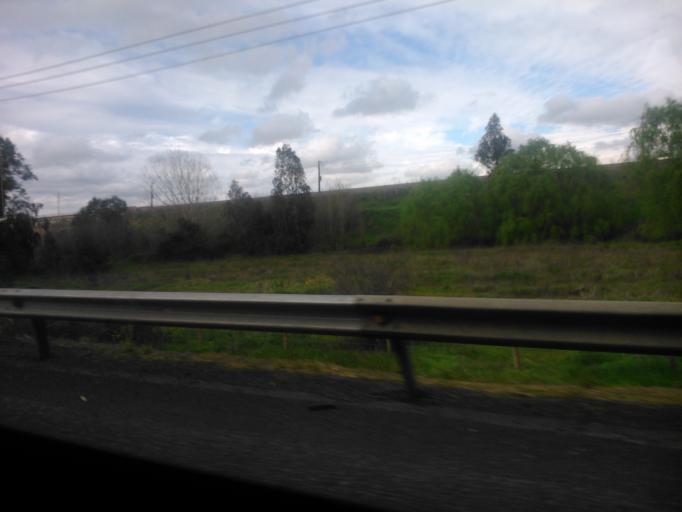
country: CL
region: Maule
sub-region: Provincia de Talca
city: Talca
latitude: -35.3541
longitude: -71.5768
